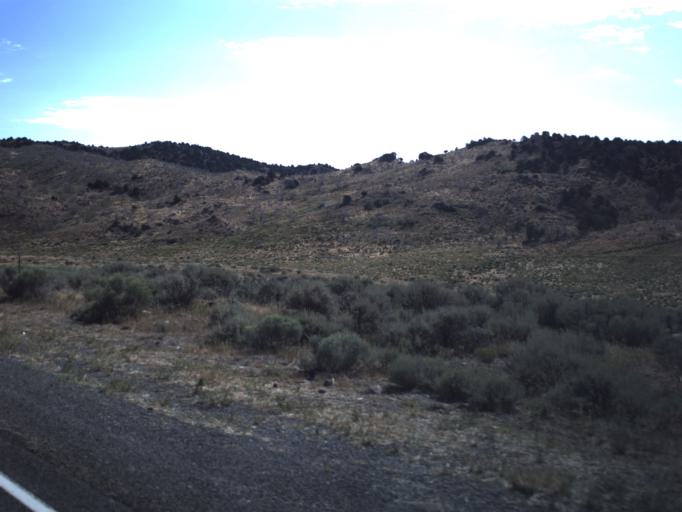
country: US
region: Utah
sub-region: Utah County
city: Genola
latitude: 39.9659
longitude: -112.0930
